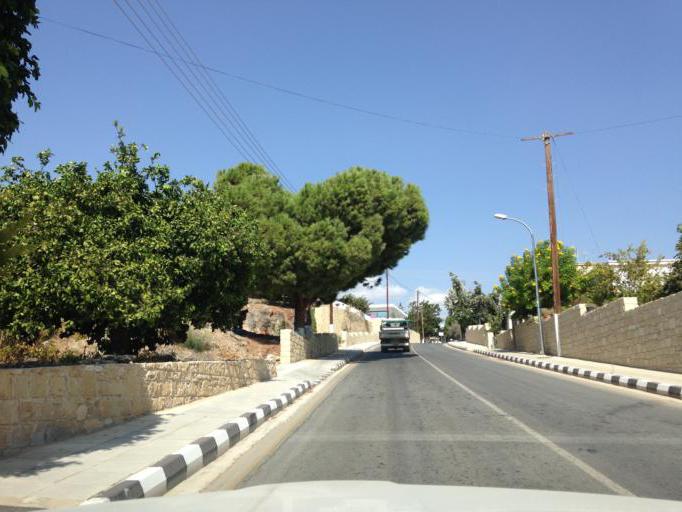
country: CY
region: Limassol
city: Pissouri
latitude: 34.7090
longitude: 32.5718
